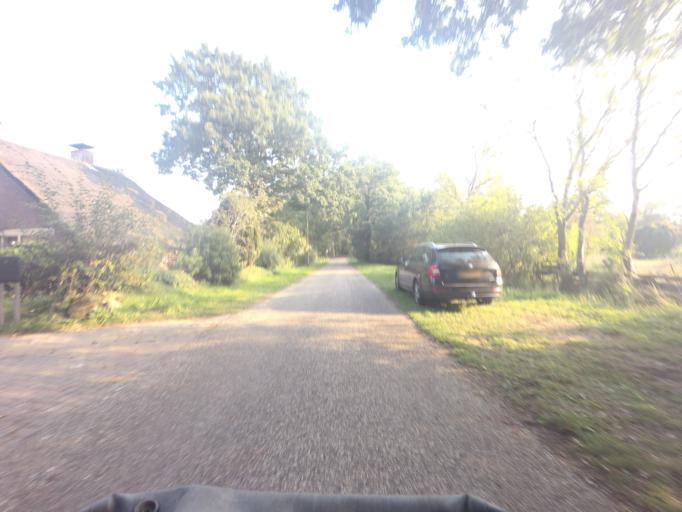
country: NL
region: Drenthe
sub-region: Gemeente Tynaarlo
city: Vries
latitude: 53.1090
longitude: 6.5248
